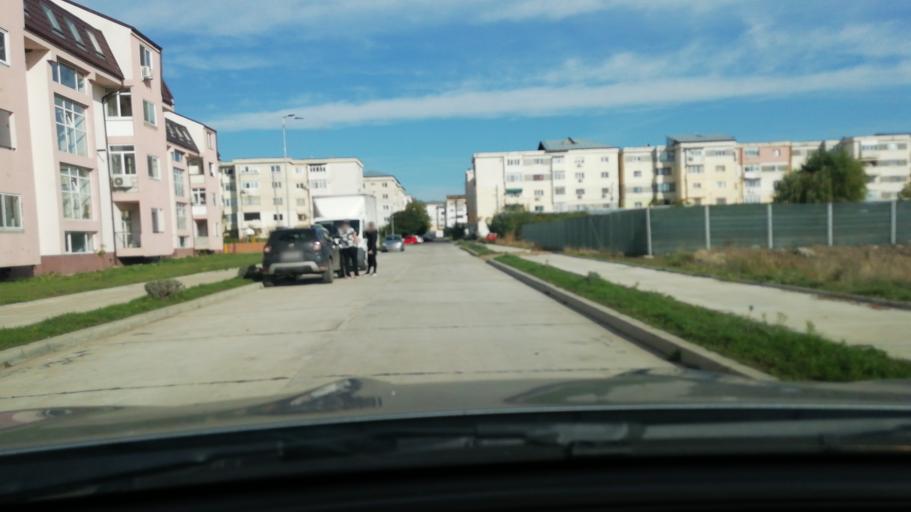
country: RO
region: Galati
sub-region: Municipiul Tecuci
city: Tecuci
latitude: 45.8261
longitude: 27.4391
